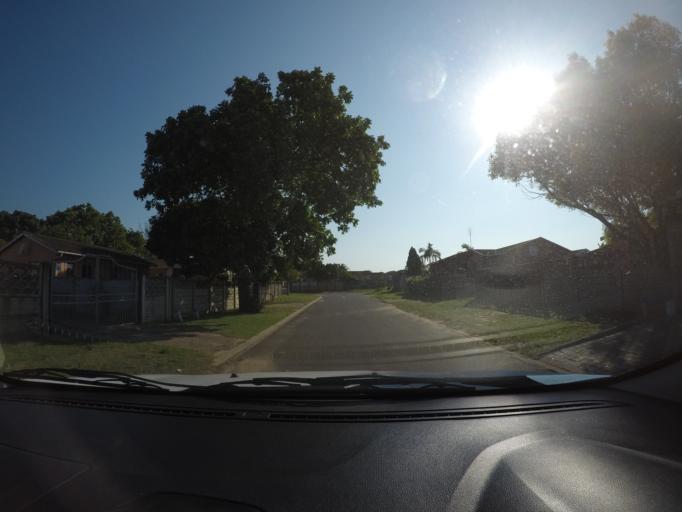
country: ZA
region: KwaZulu-Natal
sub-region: uThungulu District Municipality
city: Richards Bay
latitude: -28.7144
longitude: 32.0392
